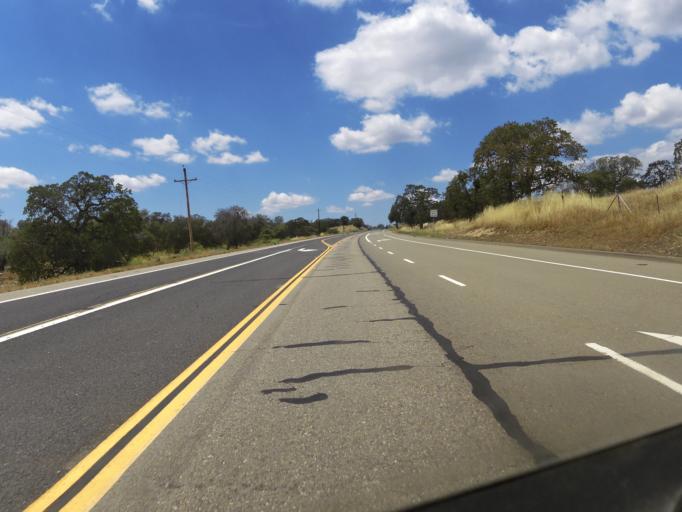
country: US
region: California
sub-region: Madera County
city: Yosemite Lakes
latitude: 37.1214
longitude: -119.7278
